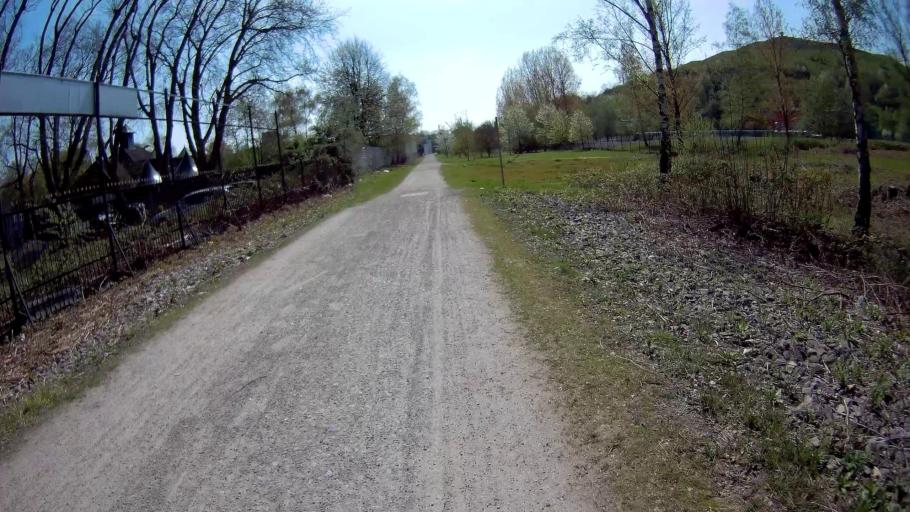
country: DE
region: North Rhine-Westphalia
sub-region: Regierungsbezirk Munster
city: Gladbeck
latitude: 51.5646
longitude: 7.0457
